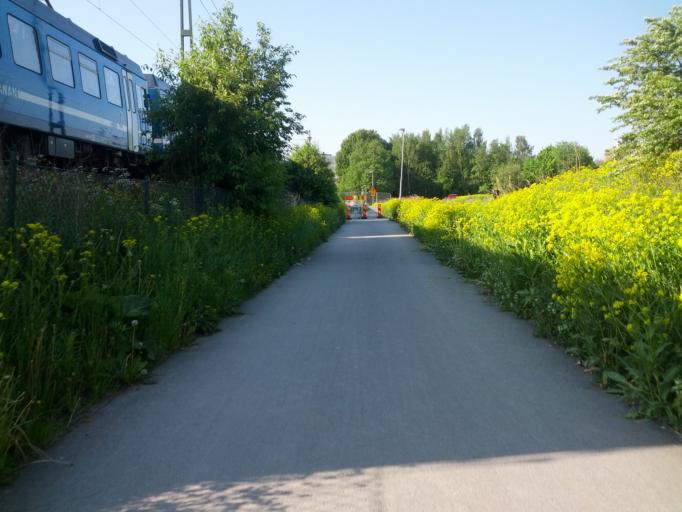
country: SE
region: Stockholm
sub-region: Taby Kommun
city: Taby
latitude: 59.4395
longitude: 18.0608
